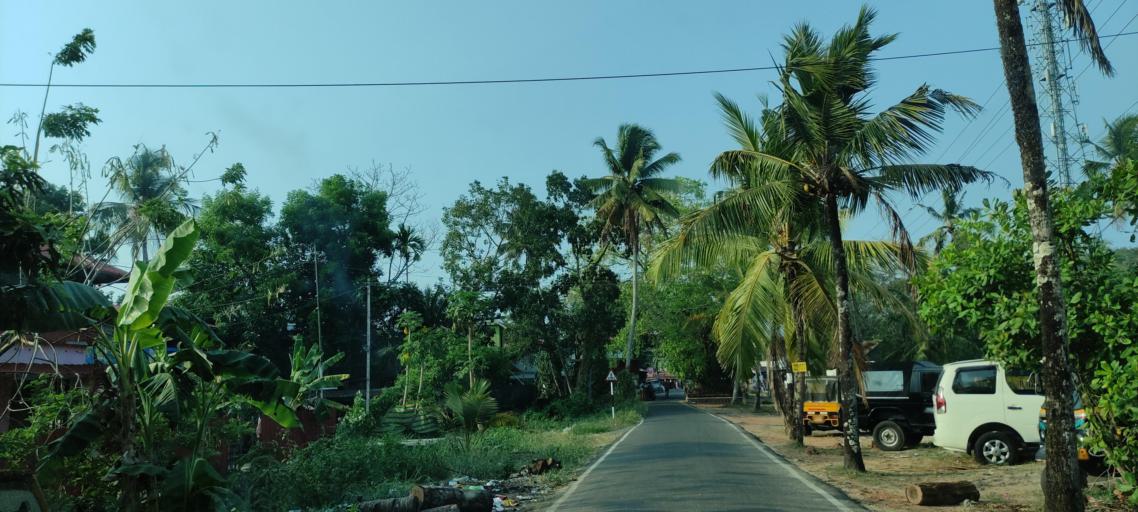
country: IN
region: Kerala
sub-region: Alappuzha
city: Alleppey
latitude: 9.5202
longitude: 76.3226
